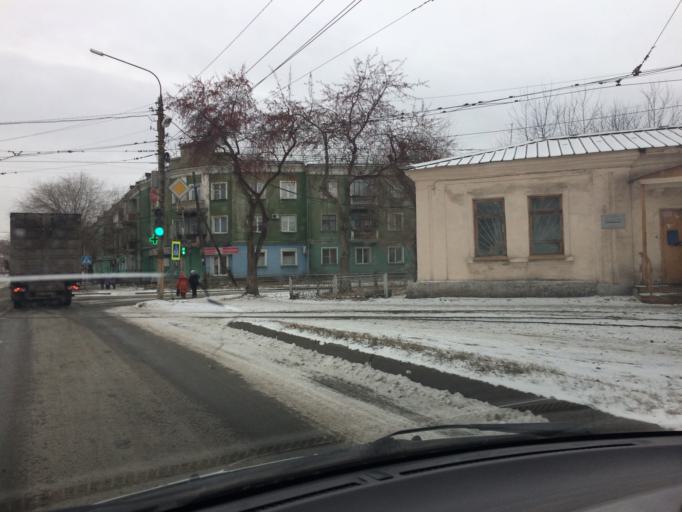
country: RU
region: Chelyabinsk
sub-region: Gorod Magnitogorsk
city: Magnitogorsk
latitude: 53.3862
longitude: 59.0729
